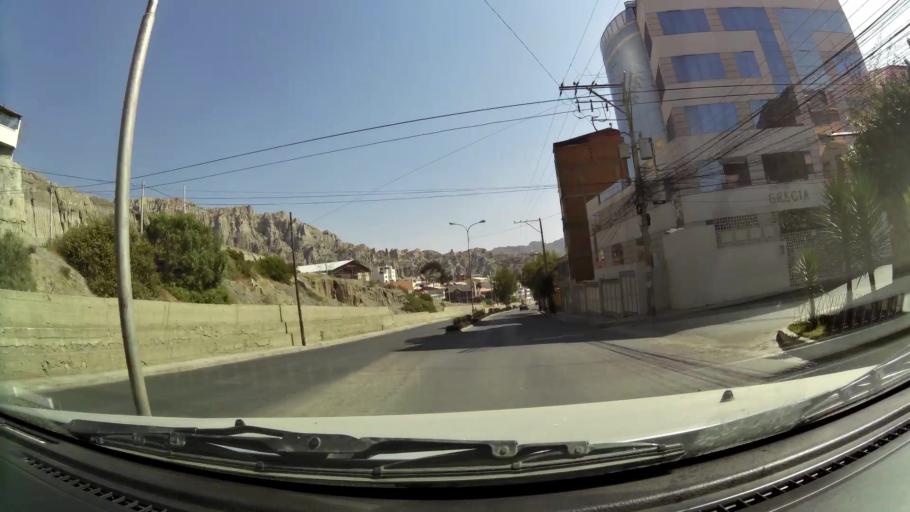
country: BO
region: La Paz
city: La Paz
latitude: -16.5468
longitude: -68.0722
